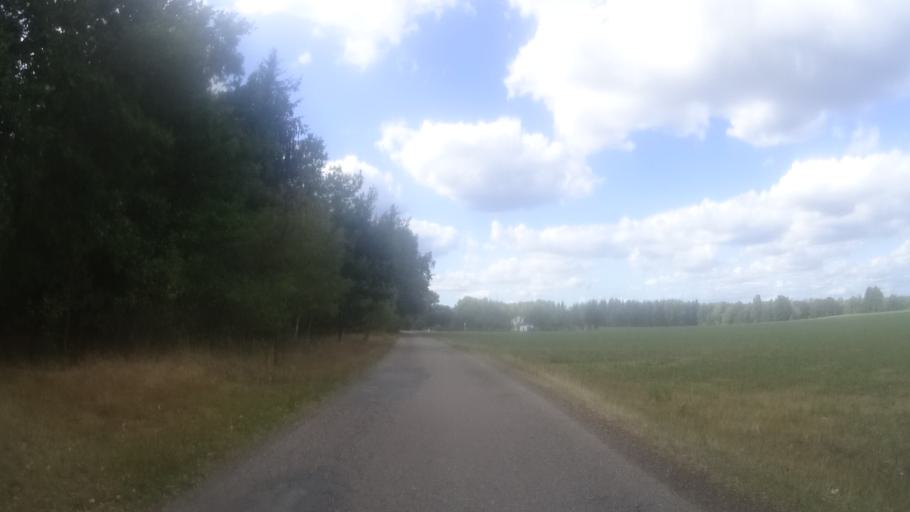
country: CZ
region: Pardubicky
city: Horni Jeleni
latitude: 50.0573
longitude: 16.1490
